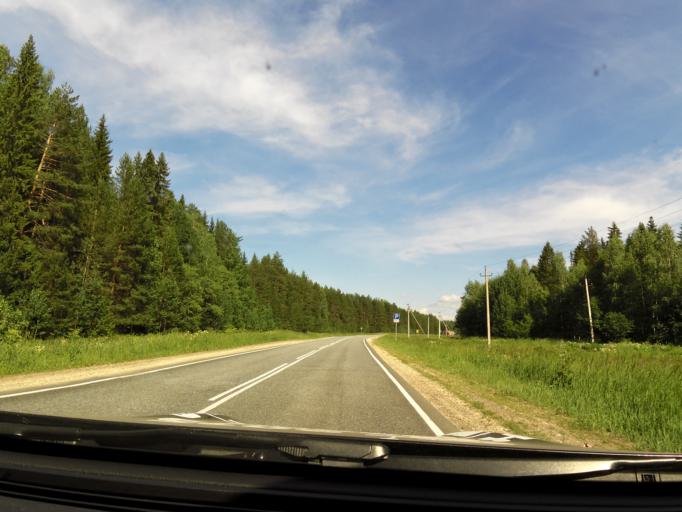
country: RU
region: Kirov
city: Belaya Kholunitsa
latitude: 58.8297
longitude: 50.6652
